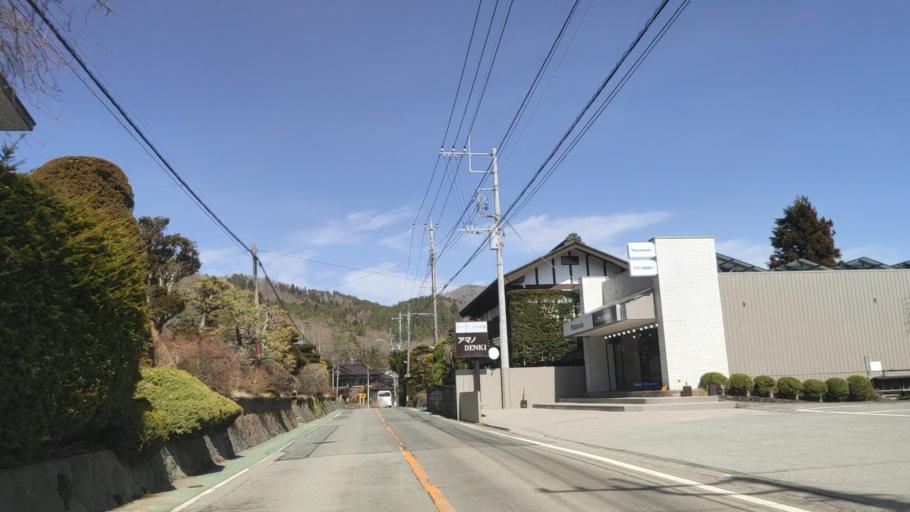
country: JP
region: Yamanashi
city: Fujikawaguchiko
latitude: 35.4618
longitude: 138.8309
